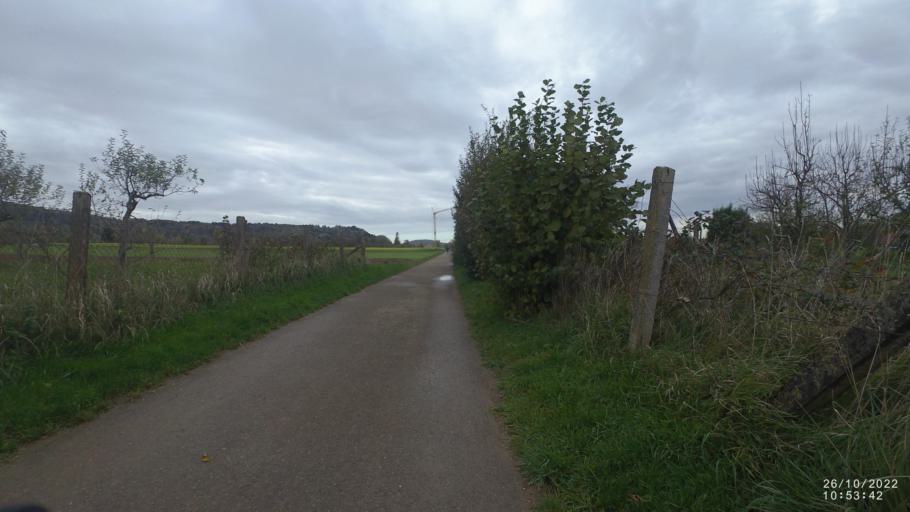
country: DE
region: Baden-Wuerttemberg
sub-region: Regierungsbezirk Stuttgart
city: Durnau
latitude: 48.6402
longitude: 9.6430
